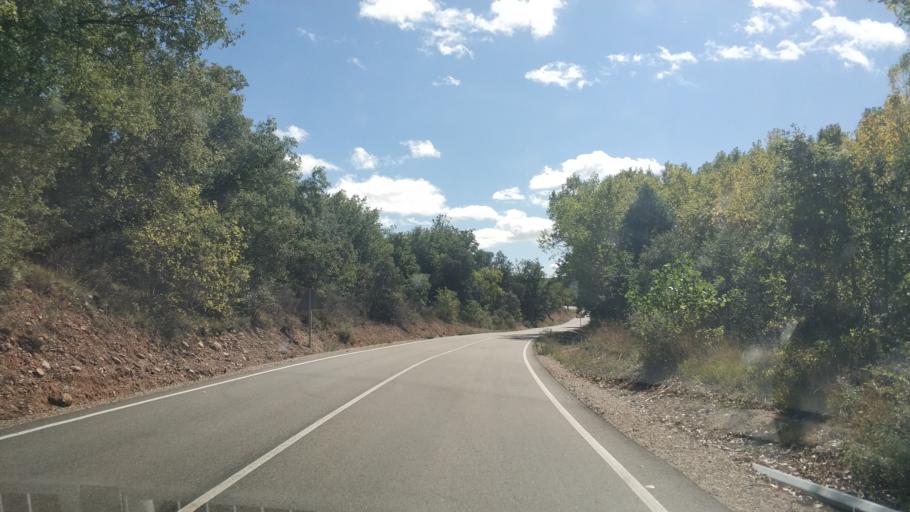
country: ES
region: Castille and Leon
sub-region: Provincia de Burgos
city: Covarrubias
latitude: 42.0502
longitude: -3.5507
